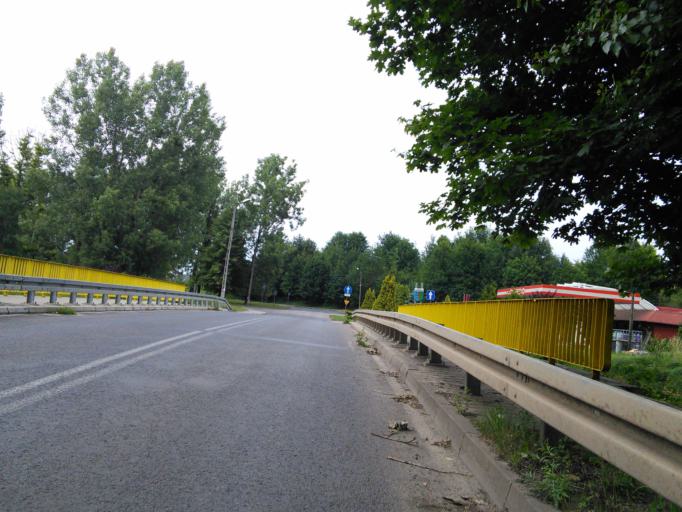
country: PL
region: Silesian Voivodeship
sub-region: Powiat bedzinski
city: Bobrowniki
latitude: 50.3717
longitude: 18.9769
